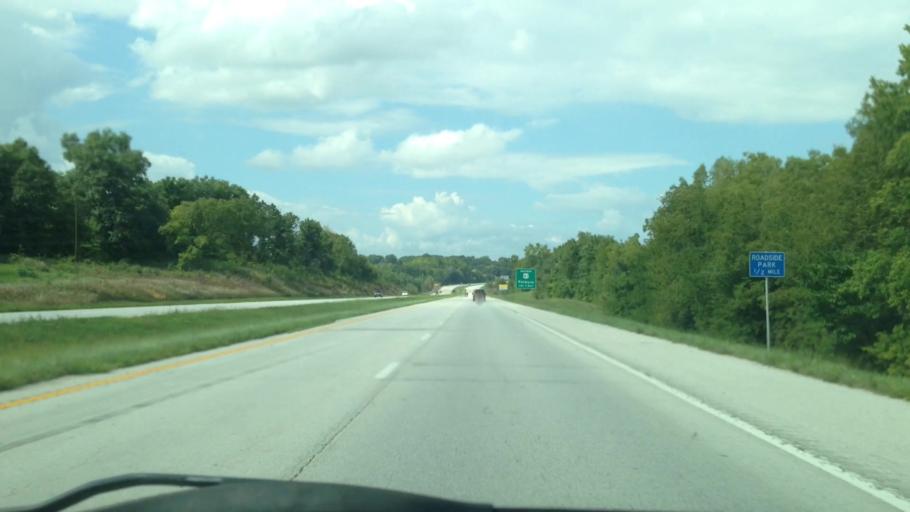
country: US
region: Missouri
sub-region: Marion County
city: Palmyra
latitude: 39.7514
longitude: -91.5177
